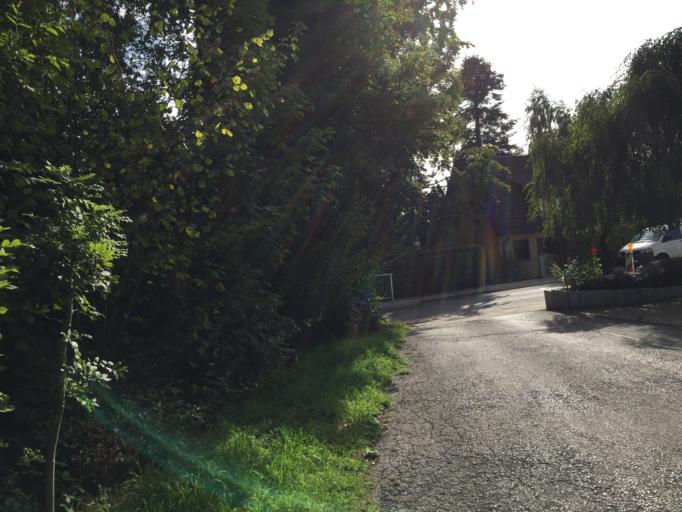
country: DE
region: North Rhine-Westphalia
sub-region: Regierungsbezirk Dusseldorf
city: Heiligenhaus
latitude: 51.3279
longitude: 6.9619
